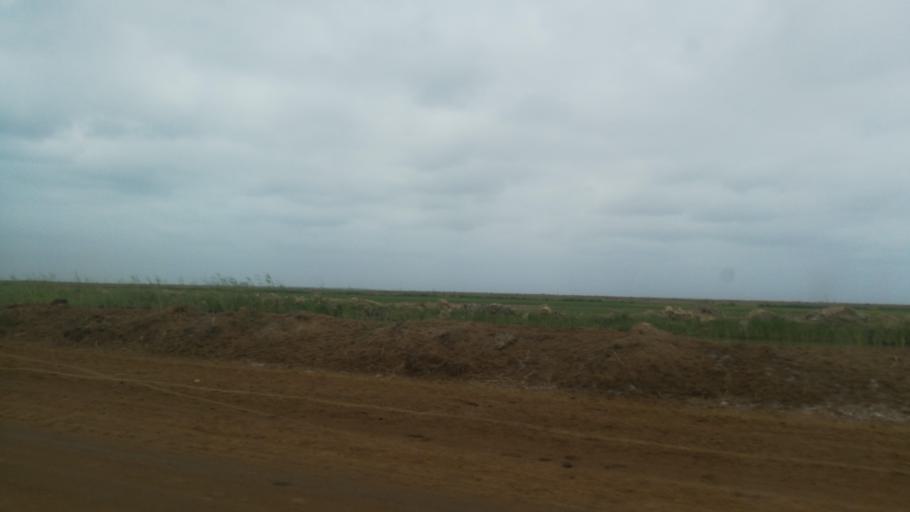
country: SN
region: Saint-Louis
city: Saint-Louis
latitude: 16.3174
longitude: -16.2347
